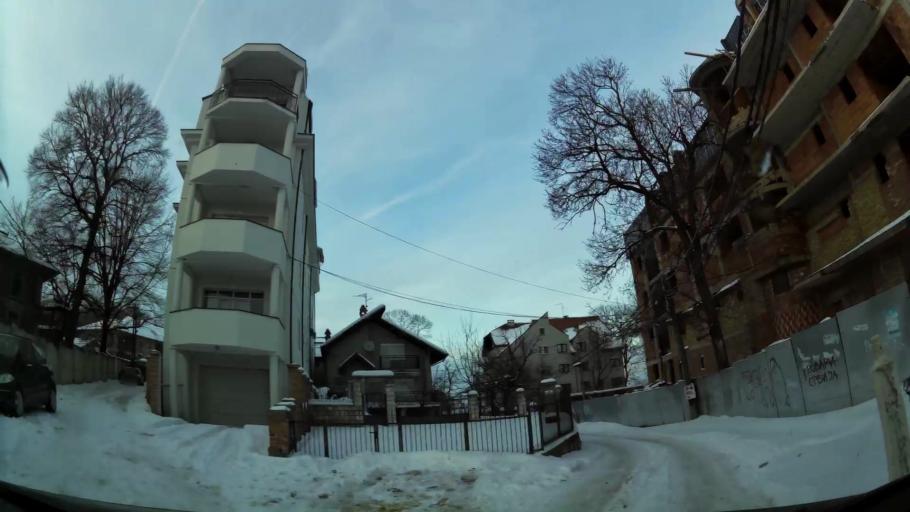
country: RS
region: Central Serbia
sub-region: Belgrade
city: Palilula
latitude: 44.7944
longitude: 20.5168
